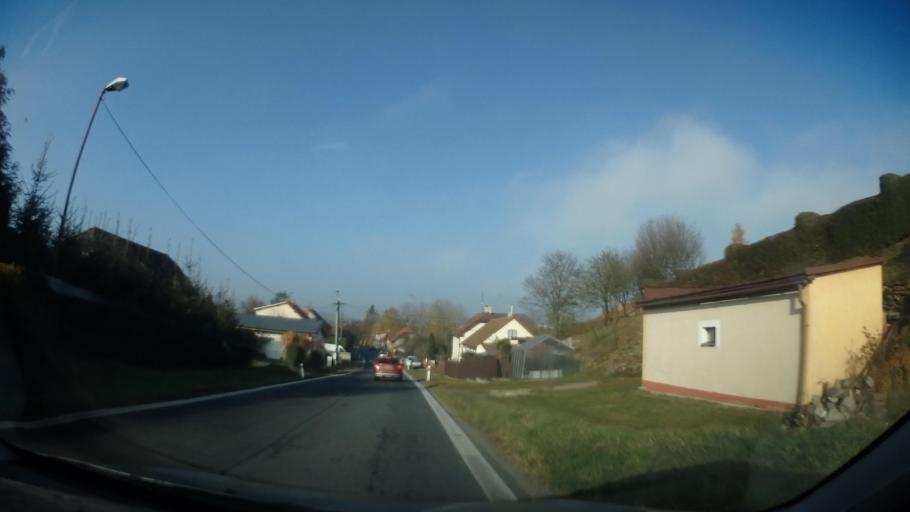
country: CZ
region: Vysocina
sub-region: Okres Zd'ar nad Sazavou
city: Nove Veseli
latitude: 49.4875
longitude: 15.9957
